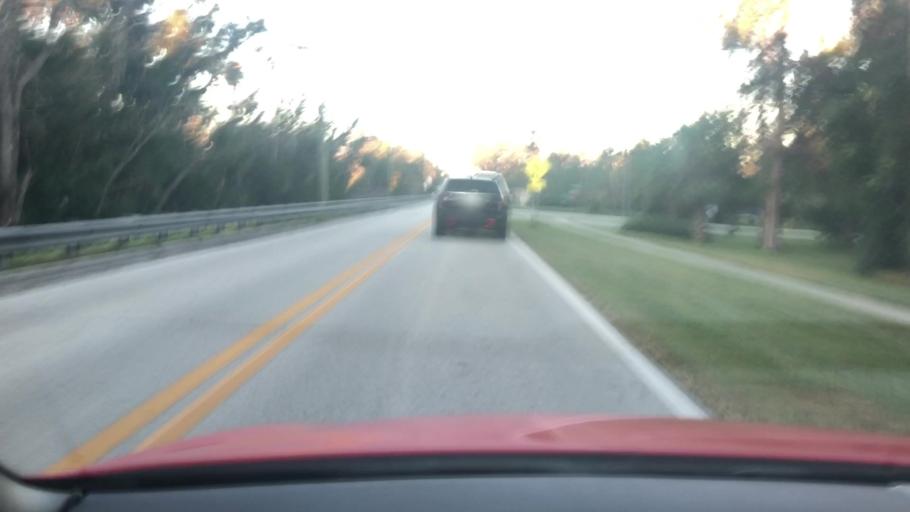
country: US
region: Florida
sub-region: Volusia County
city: South Daytona
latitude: 29.1586
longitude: -81.0053
